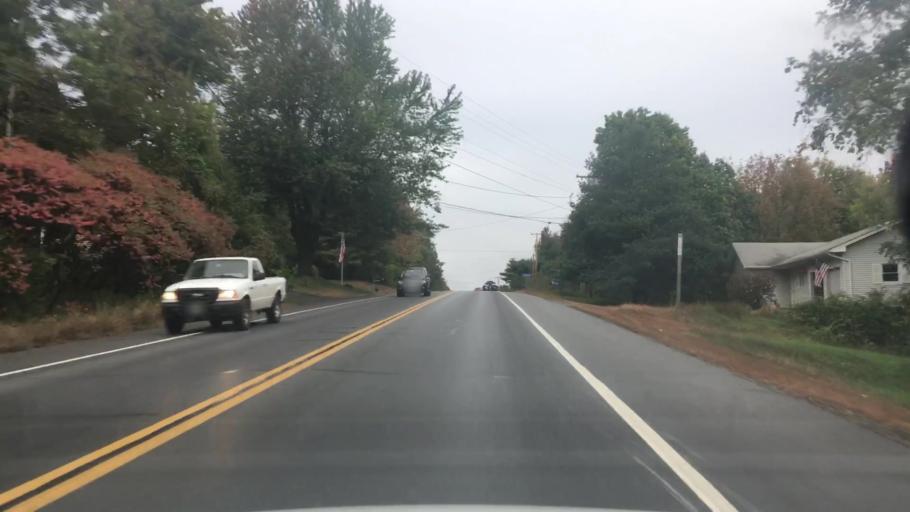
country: US
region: Maine
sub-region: Kennebec County
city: Belgrade
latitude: 44.3890
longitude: -69.8026
